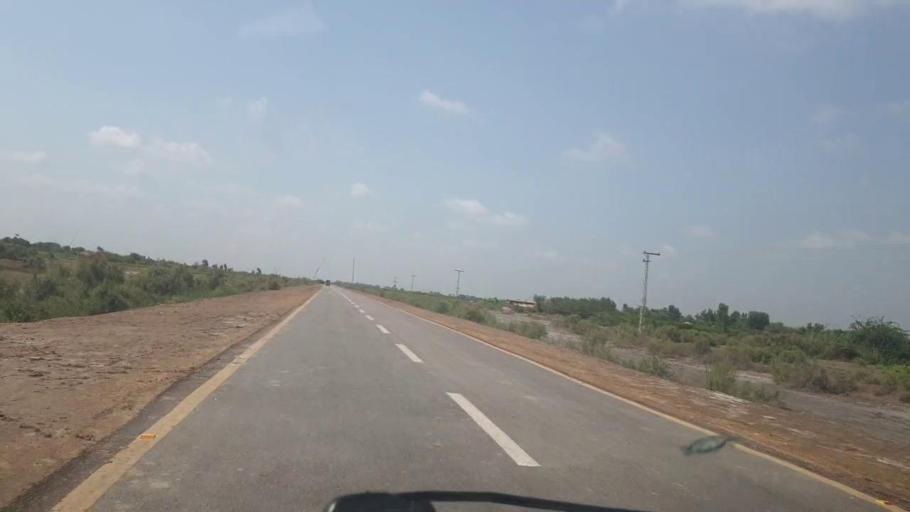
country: PK
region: Sindh
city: Berani
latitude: 25.7260
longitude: 68.9445
